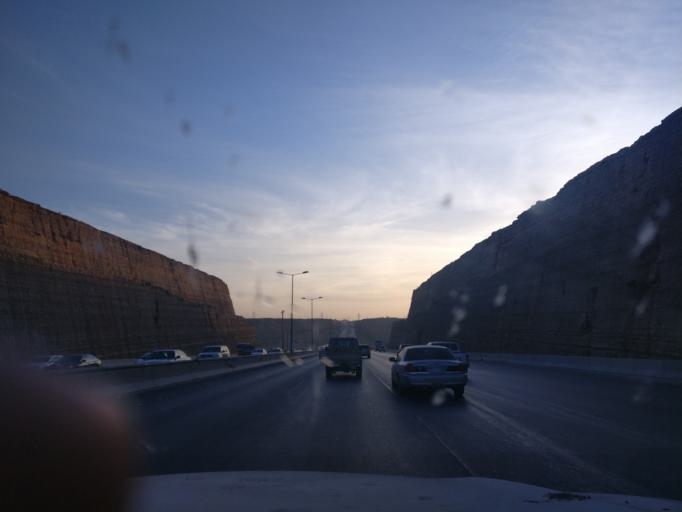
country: SA
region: Ar Riyad
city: Riyadh
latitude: 24.6188
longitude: 46.5724
